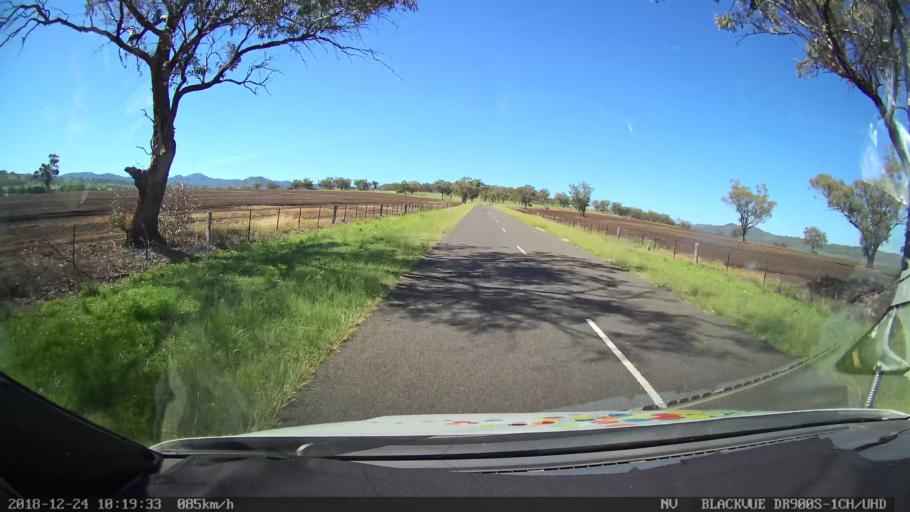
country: AU
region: New South Wales
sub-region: Liverpool Plains
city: Quirindi
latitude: -31.7318
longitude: 150.5649
